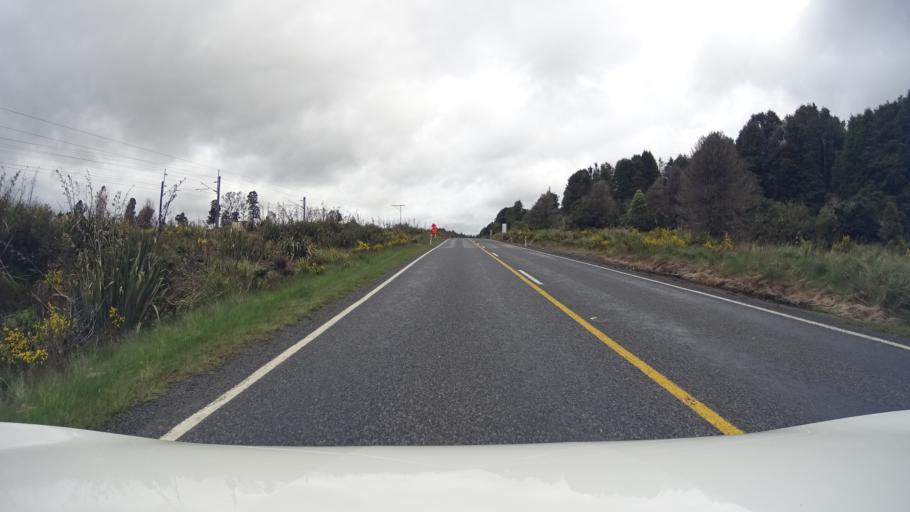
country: NZ
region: Manawatu-Wanganui
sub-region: Ruapehu District
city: Waiouru
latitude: -39.2604
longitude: 175.3890
